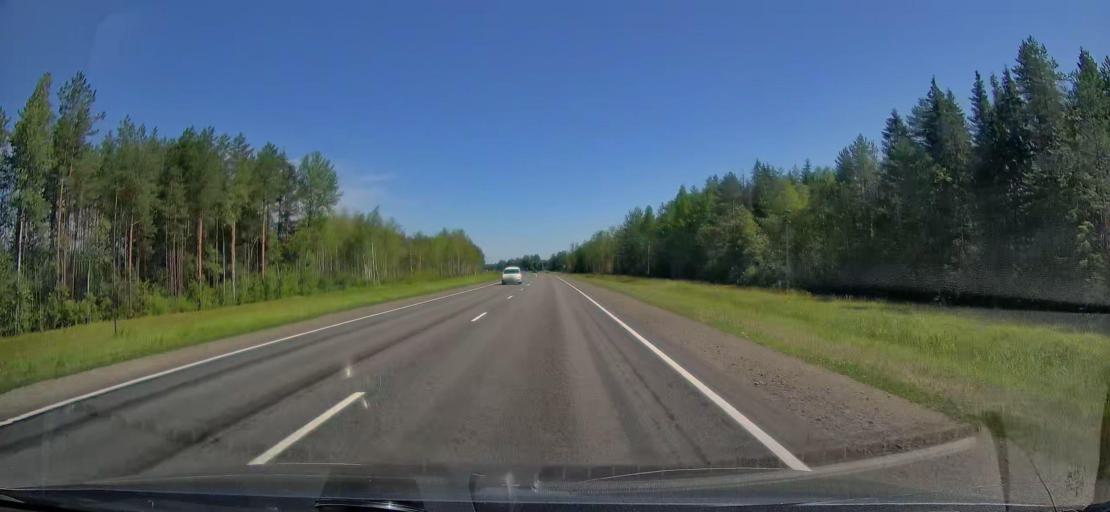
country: RU
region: Tverskaya
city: Ves'yegonsk
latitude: 58.9236
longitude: 37.2346
